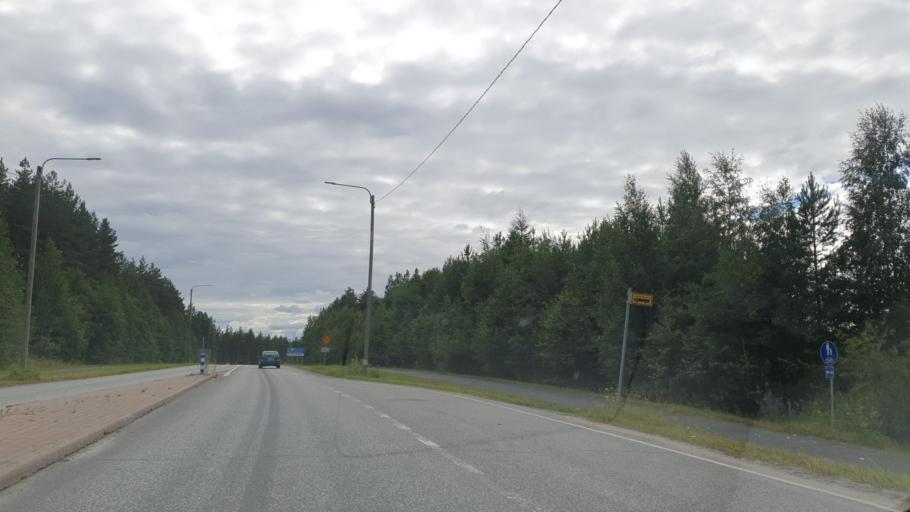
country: FI
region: Northern Savo
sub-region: Ylae-Savo
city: Iisalmi
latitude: 63.5219
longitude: 27.2420
